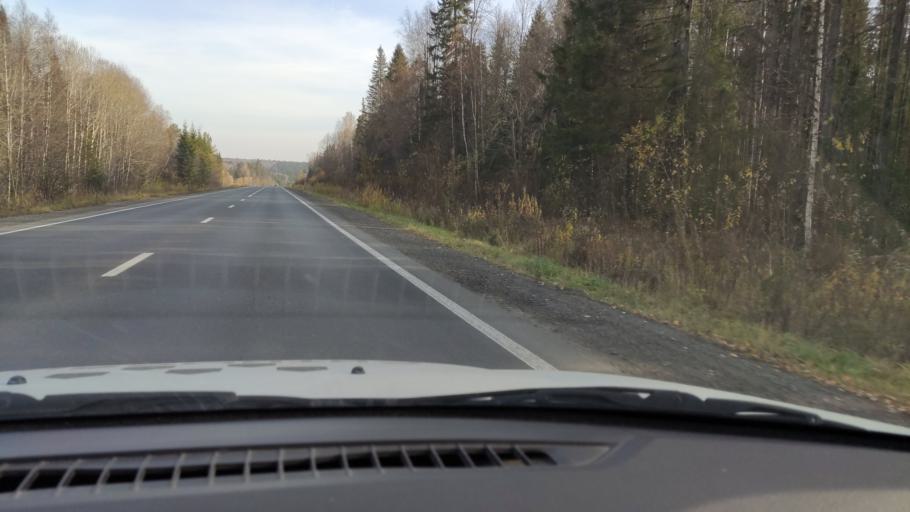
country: RU
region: Perm
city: Novyye Lyady
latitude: 58.0419
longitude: 56.4512
